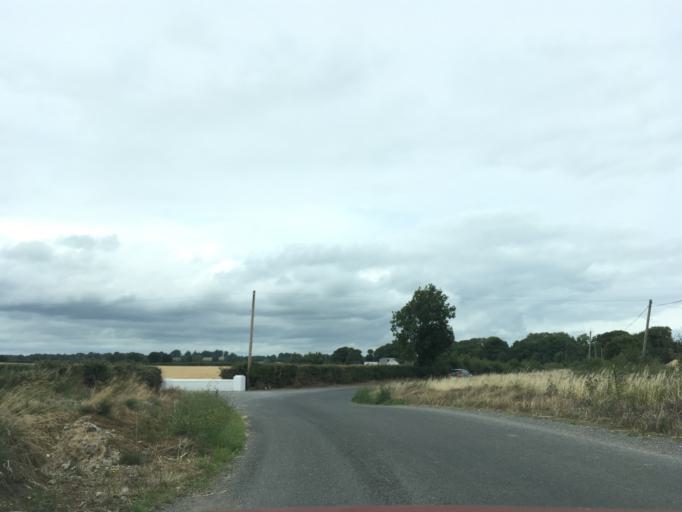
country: IE
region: Munster
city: Cahir
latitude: 52.4630
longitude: -8.0059
